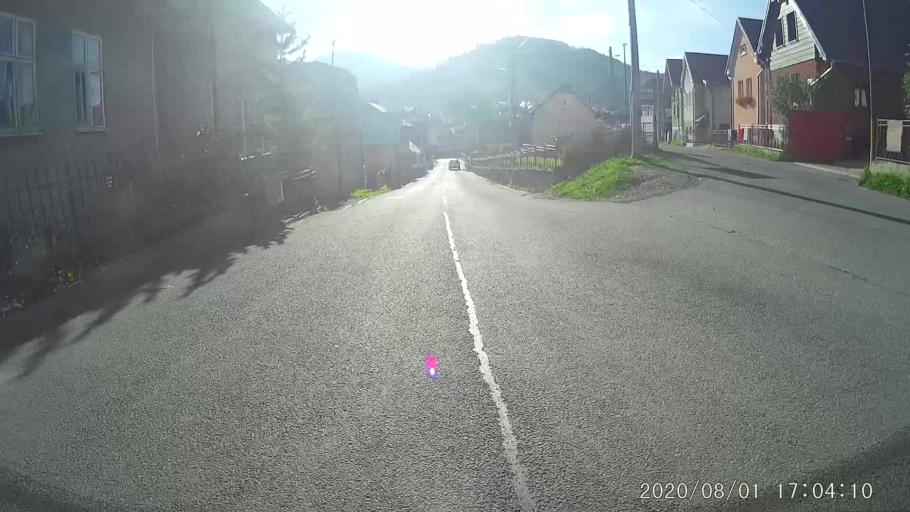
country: SK
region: Presovsky
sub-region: Okres Poprad
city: Zdiar
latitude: 49.2341
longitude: 20.3575
